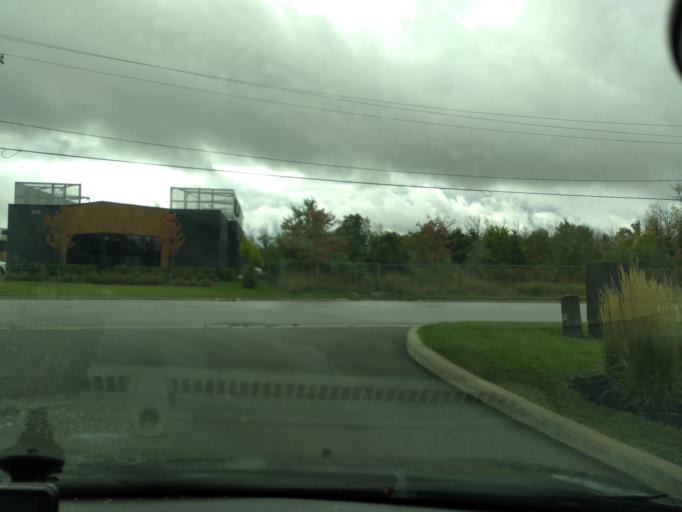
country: CA
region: Ontario
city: Innisfil
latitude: 44.3276
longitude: -79.6991
